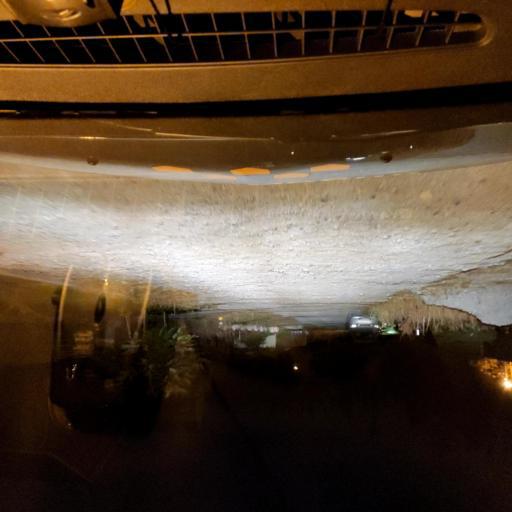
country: RU
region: Voronezj
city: Somovo
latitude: 51.7181
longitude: 39.3201
